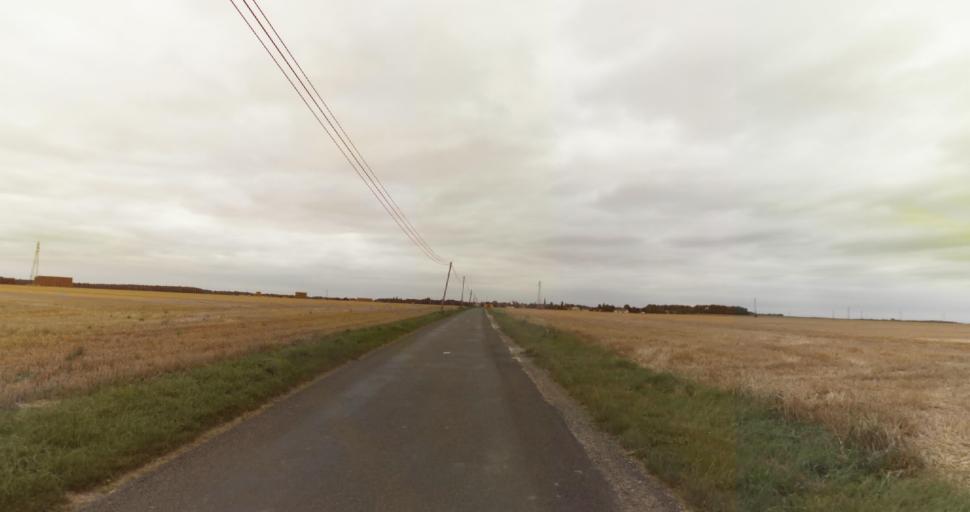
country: FR
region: Haute-Normandie
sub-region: Departement de l'Eure
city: Menilles
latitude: 48.9470
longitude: 1.2656
